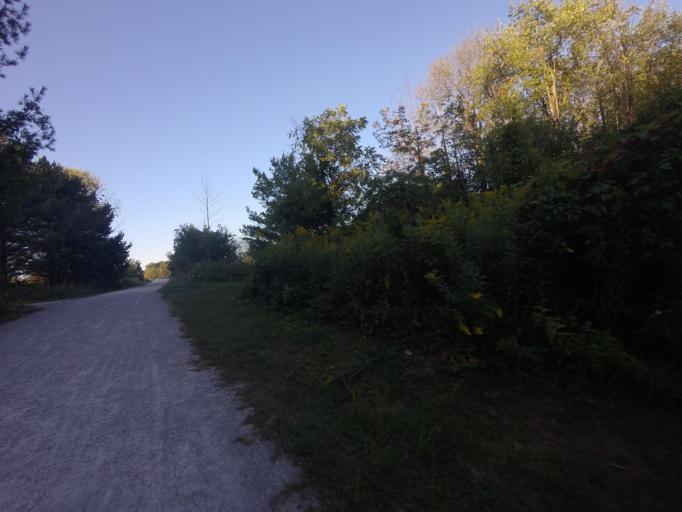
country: CA
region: Ontario
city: Brampton
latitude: 43.8731
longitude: -79.8595
